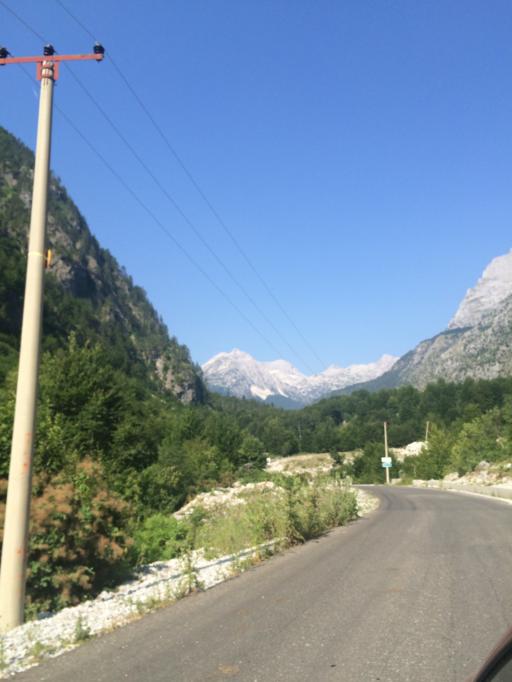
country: AL
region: Kukes
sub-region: Rrethi i Tropojes
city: Valbone
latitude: 42.4600
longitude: 19.9264
